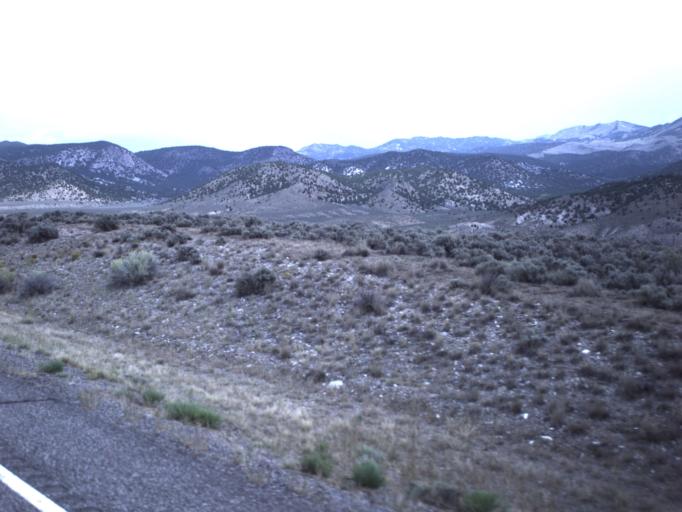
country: US
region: Utah
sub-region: Garfield County
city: Panguitch
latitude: 38.0175
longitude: -112.3682
